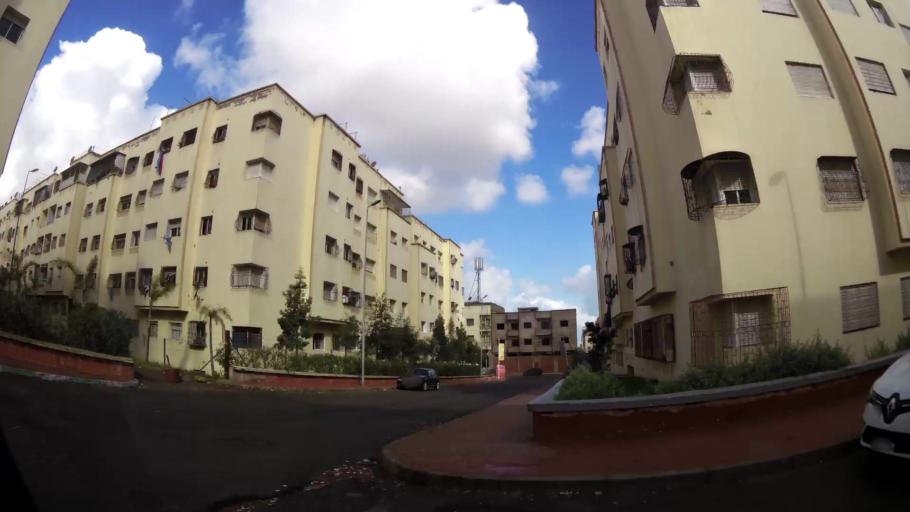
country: MA
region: Grand Casablanca
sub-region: Mediouna
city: Tit Mellil
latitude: 33.5776
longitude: -7.5299
